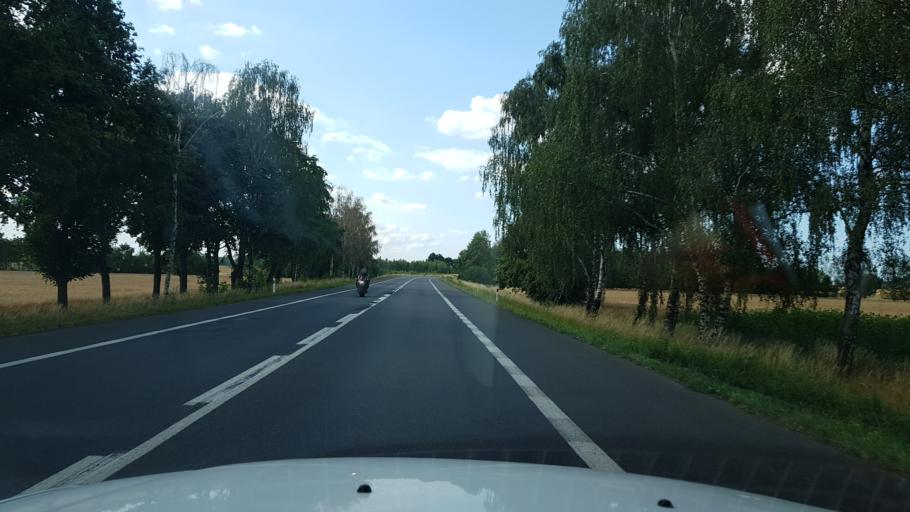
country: PL
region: West Pomeranian Voivodeship
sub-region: Powiat gryfinski
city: Stare Czarnowo
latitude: 53.2144
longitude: 14.8021
